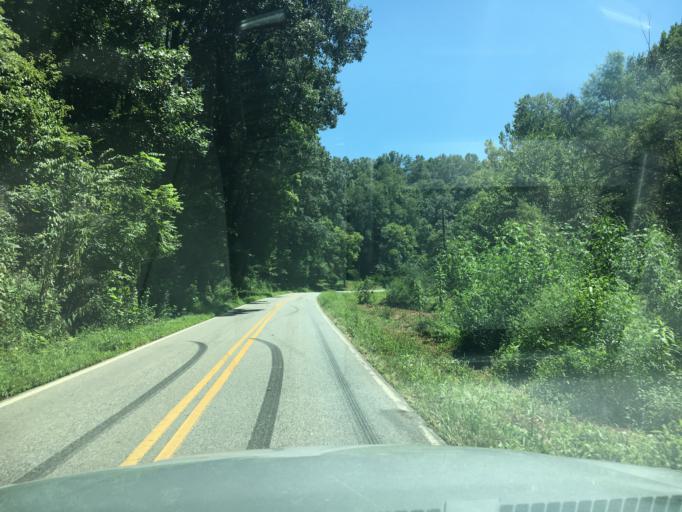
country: US
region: North Carolina
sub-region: McDowell County
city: Marion
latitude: 35.6975
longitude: -82.0455
